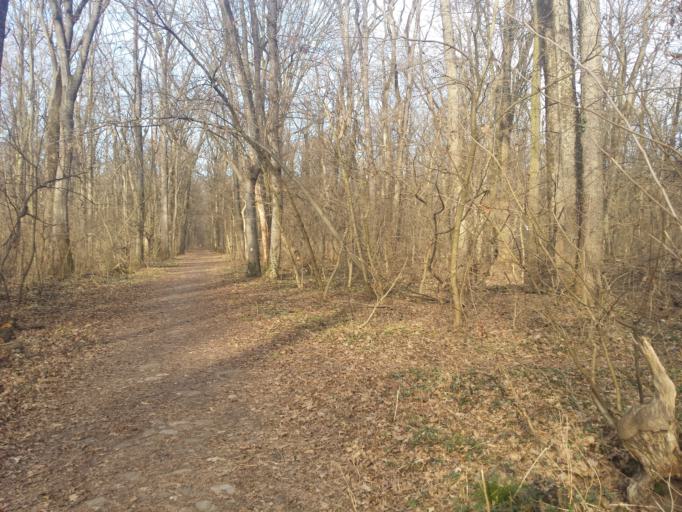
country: RO
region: Ilfov
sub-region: Comuna Otopeni
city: Otopeni
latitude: 44.5223
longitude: 26.0917
